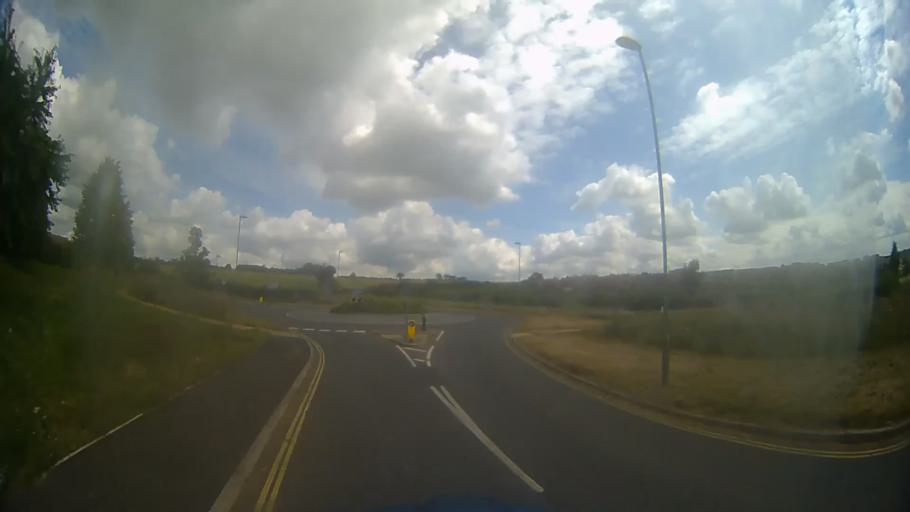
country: GB
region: England
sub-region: Hampshire
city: Andover
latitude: 51.2286
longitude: -1.4609
